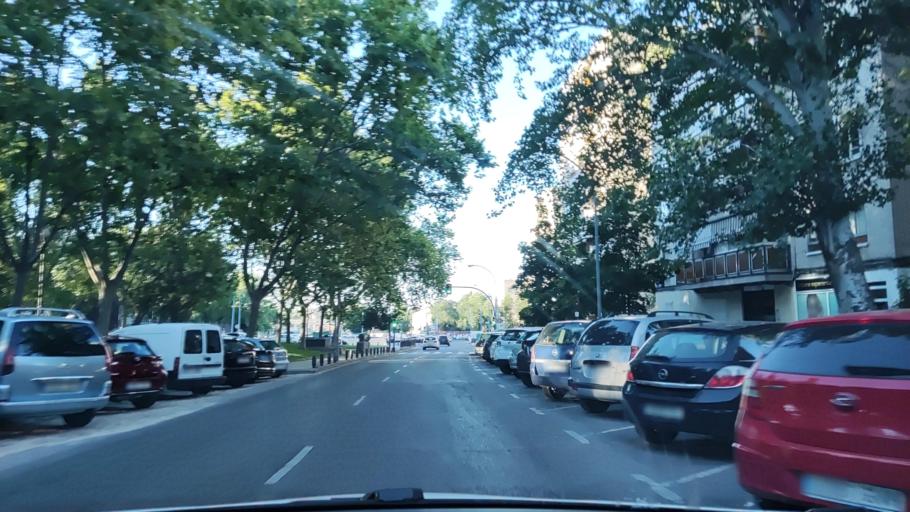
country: ES
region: Madrid
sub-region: Provincia de Madrid
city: Leganes
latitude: 40.3371
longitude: -3.7565
